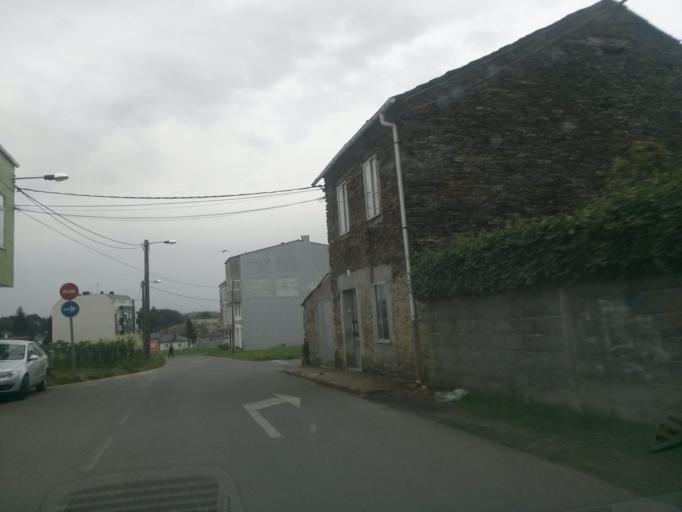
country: ES
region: Galicia
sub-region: Provincia de Lugo
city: Lugo
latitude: 43.0293
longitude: -7.5657
